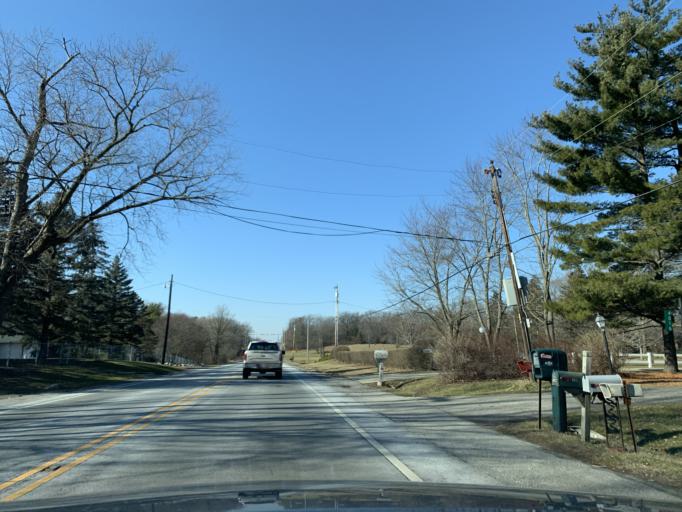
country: US
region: Indiana
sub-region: Lake County
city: Crown Point
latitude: 41.4205
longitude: -87.3841
